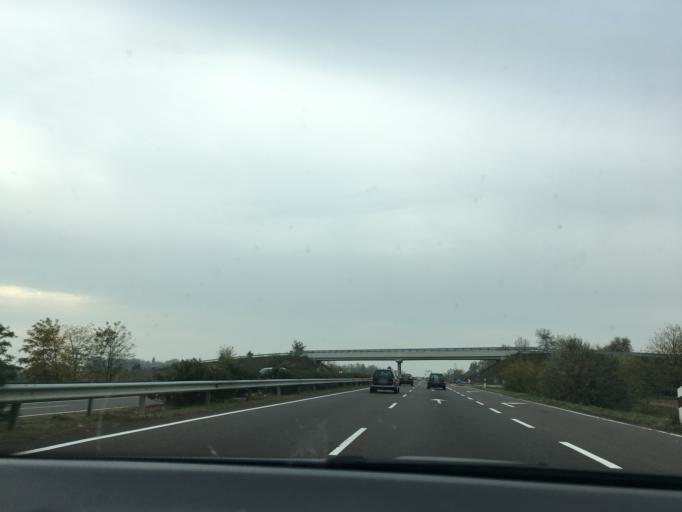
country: HU
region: Pest
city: Tortel
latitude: 47.1909
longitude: 19.9014
